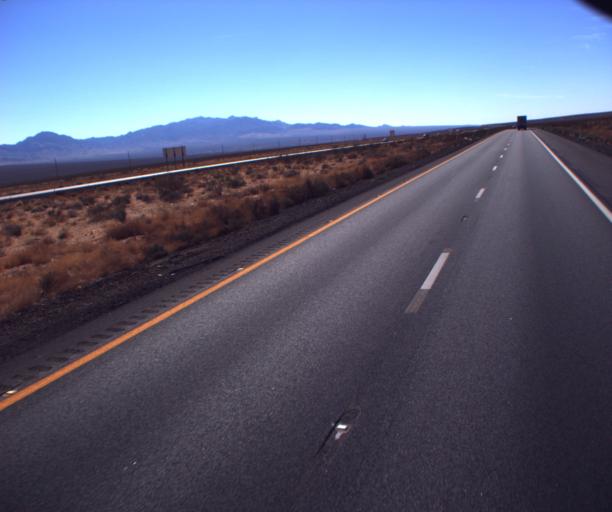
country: US
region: Arizona
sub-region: Mohave County
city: Beaver Dam
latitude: 36.8820
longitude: -113.9453
